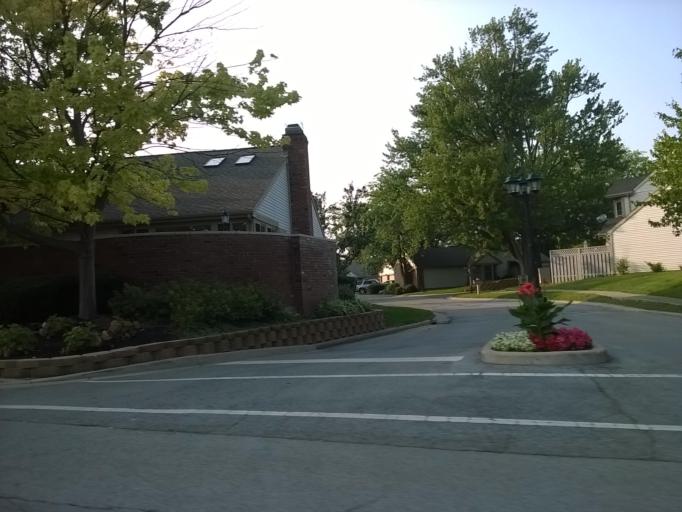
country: US
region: Indiana
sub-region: Hamilton County
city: Carmel
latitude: 39.9567
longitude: -86.1117
